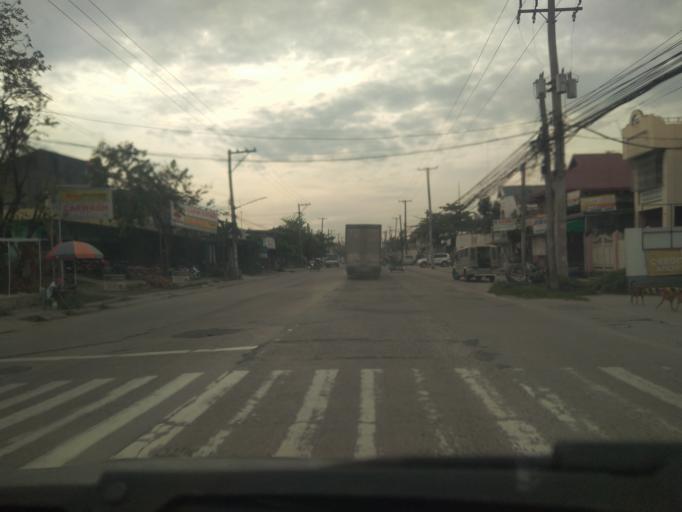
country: PH
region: Central Luzon
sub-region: Province of Pampanga
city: San Fernando
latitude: 15.0211
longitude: 120.6991
